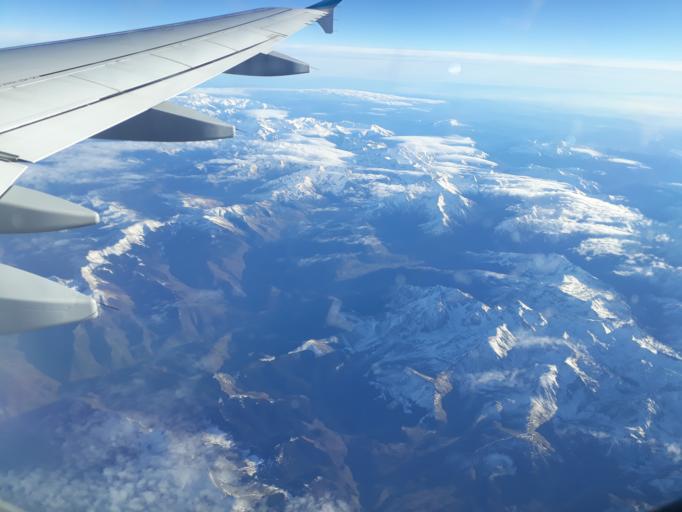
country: FR
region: Midi-Pyrenees
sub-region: Departement des Hautes-Pyrenees
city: Campan
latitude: 43.0386
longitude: 0.2063
